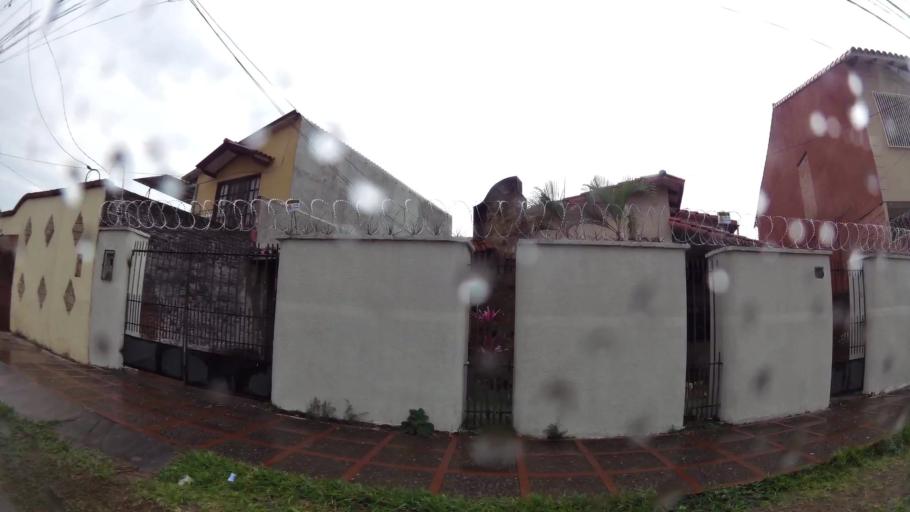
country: BO
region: Santa Cruz
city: Santa Cruz de la Sierra
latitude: -17.7925
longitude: -63.1547
